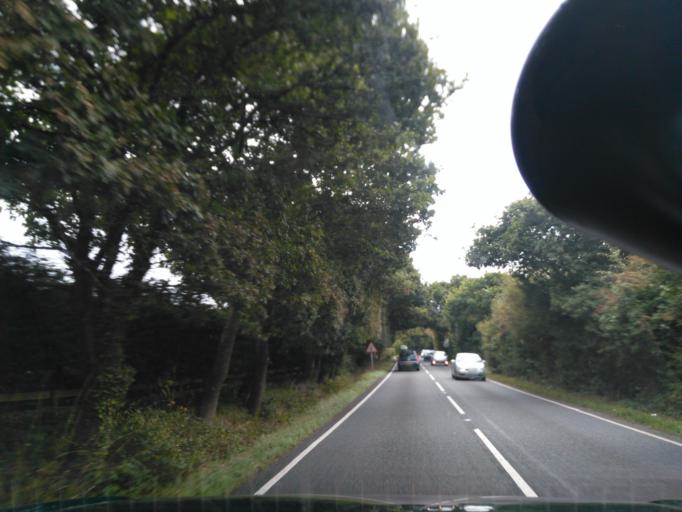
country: GB
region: England
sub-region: Dorset
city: Lytchett Matravers
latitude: 50.7398
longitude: -2.1086
